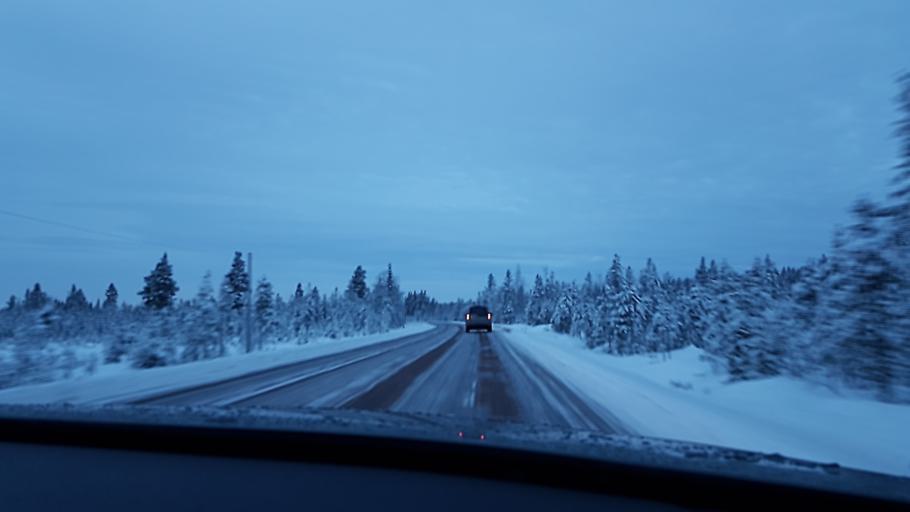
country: SE
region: Jaemtland
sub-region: Harjedalens Kommun
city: Sveg
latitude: 62.0550
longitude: 14.5484
